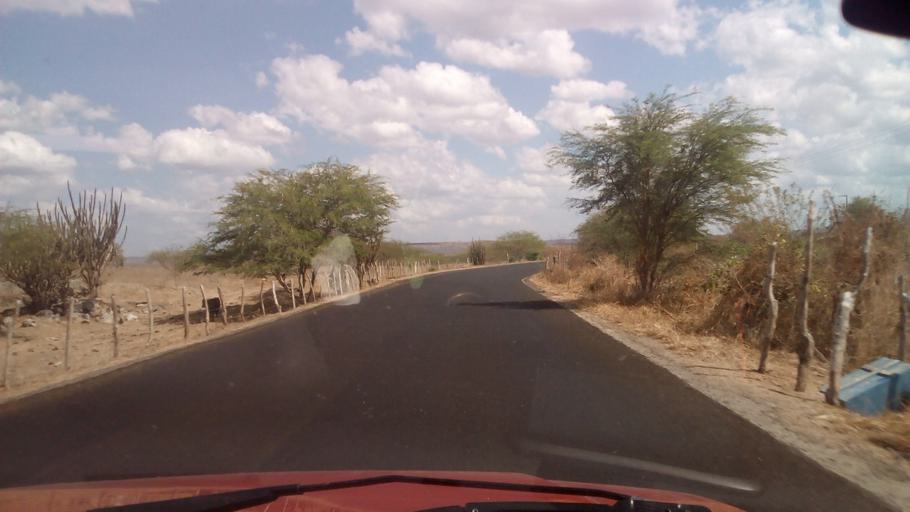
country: BR
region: Paraiba
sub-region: Cacimba De Dentro
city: Cacimba de Dentro
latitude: -6.6692
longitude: -35.7543
